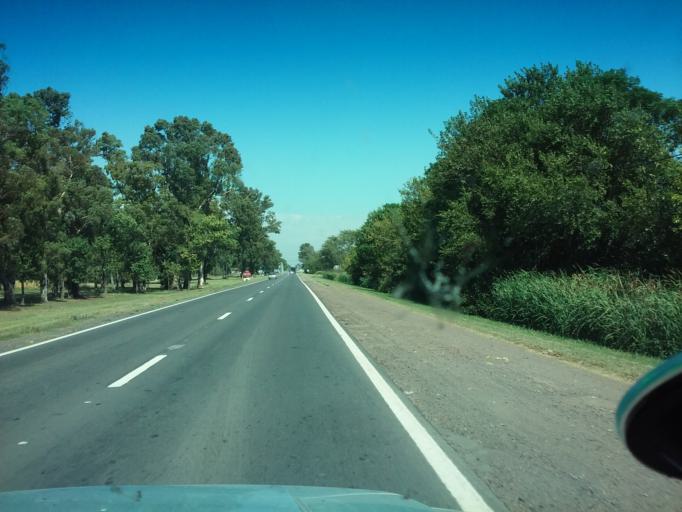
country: AR
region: Buenos Aires
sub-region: Partido de Nueve de Julio
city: Nueve de Julio
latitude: -35.4852
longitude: -60.8828
